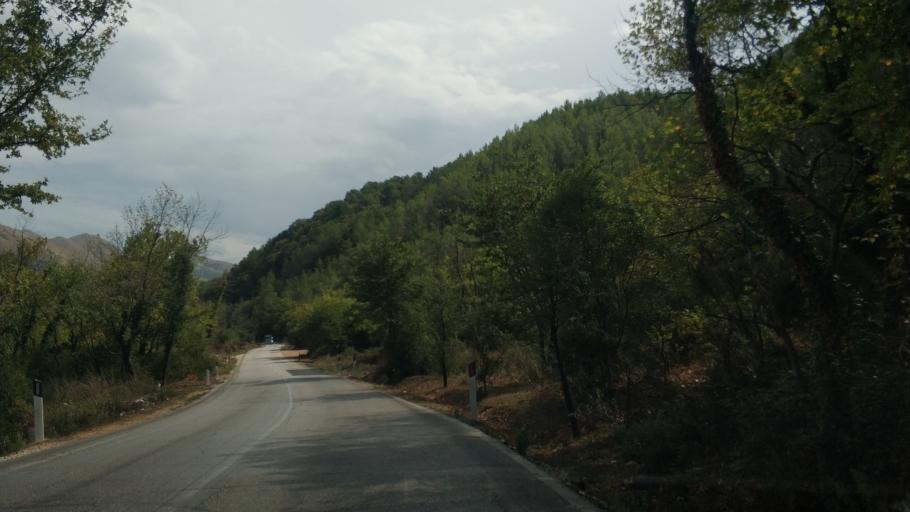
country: AL
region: Vlore
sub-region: Rrethi i Delvines
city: Delvine
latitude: 39.9214
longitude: 20.1650
